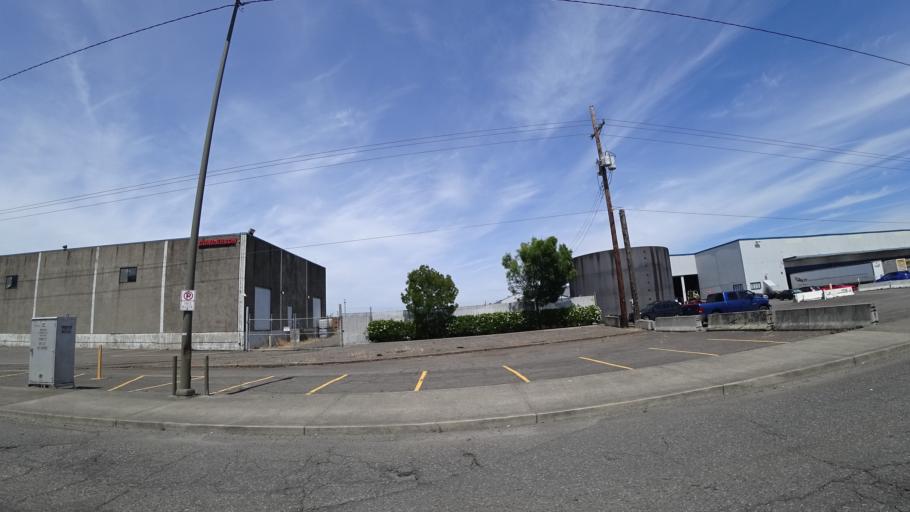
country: US
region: Oregon
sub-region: Multnomah County
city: Portland
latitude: 45.5517
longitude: -122.7145
